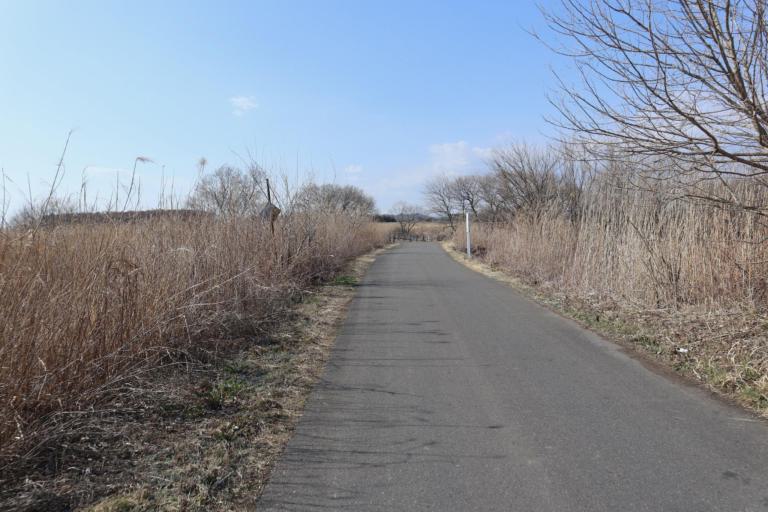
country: JP
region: Tochigi
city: Fujioka
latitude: 36.2600
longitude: 139.6862
